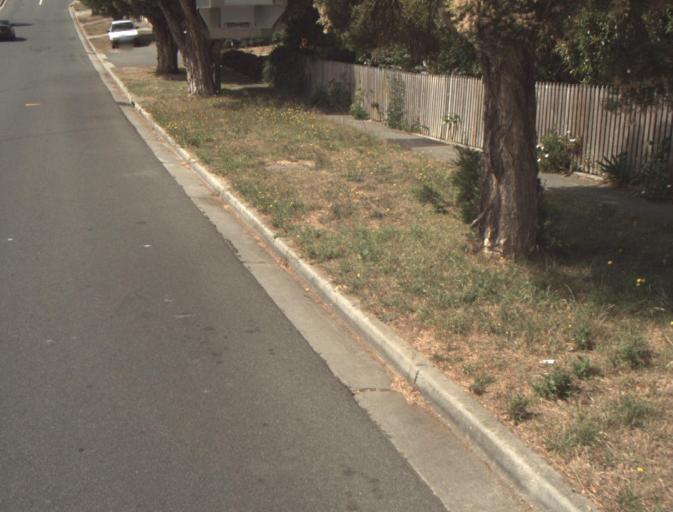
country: AU
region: Tasmania
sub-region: Launceston
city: Summerhill
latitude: -41.4657
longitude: 147.1407
